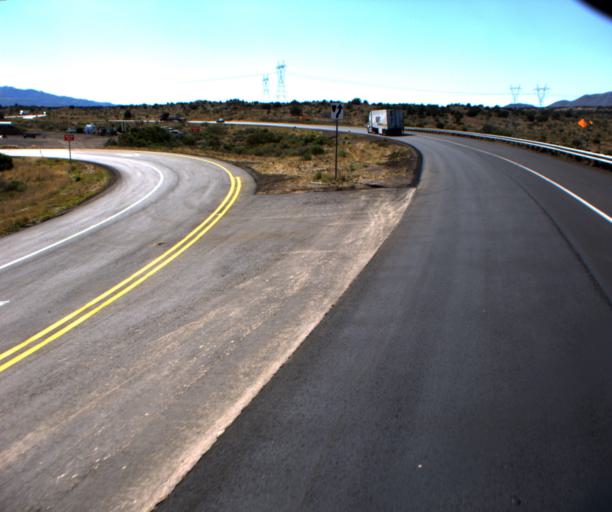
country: US
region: Arizona
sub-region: Mohave County
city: New Kingman-Butler
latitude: 35.1611
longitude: -113.6981
